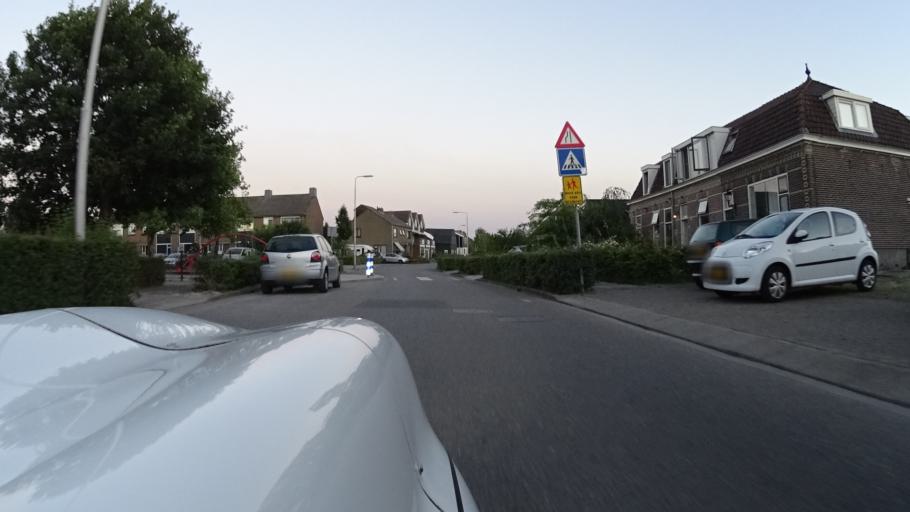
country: NL
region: South Holland
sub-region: Gemeente Kaag en Braassem
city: Oude Wetering
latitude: 52.1908
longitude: 4.6280
